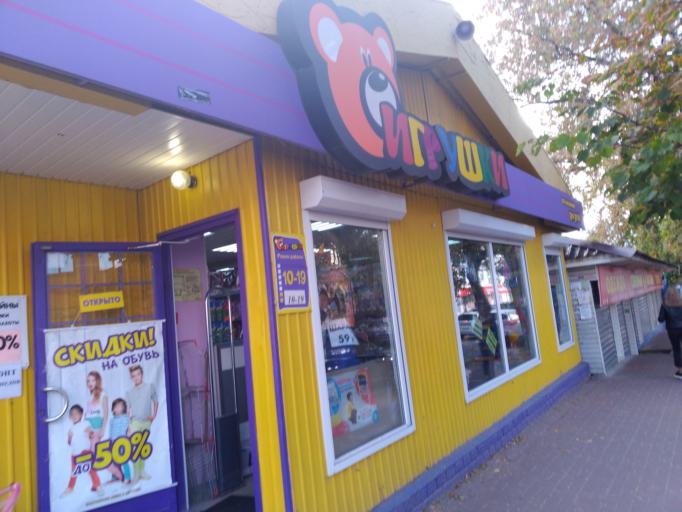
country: RU
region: Kaluga
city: Kaluga
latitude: 54.5126
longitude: 36.2563
